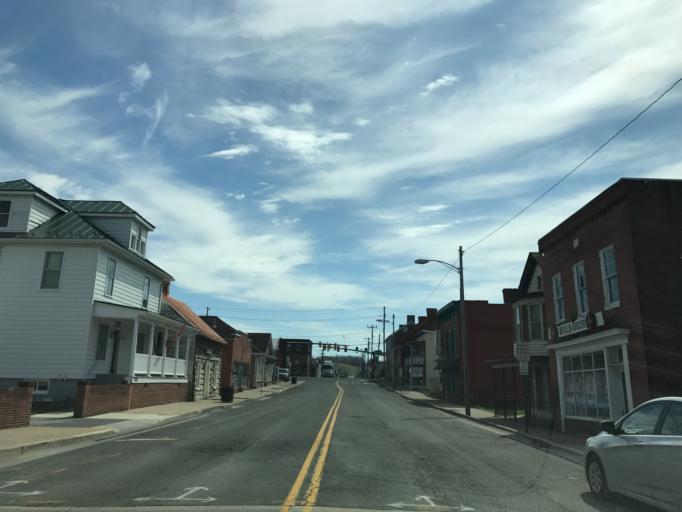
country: US
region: Virginia
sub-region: Shenandoah County
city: Strasburg
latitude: 38.9889
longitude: -78.3603
